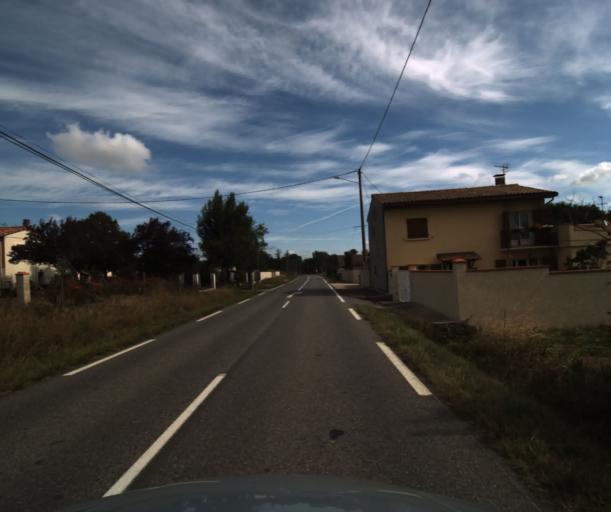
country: FR
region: Midi-Pyrenees
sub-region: Departement de la Haute-Garonne
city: Seysses
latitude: 43.4691
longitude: 1.3021
